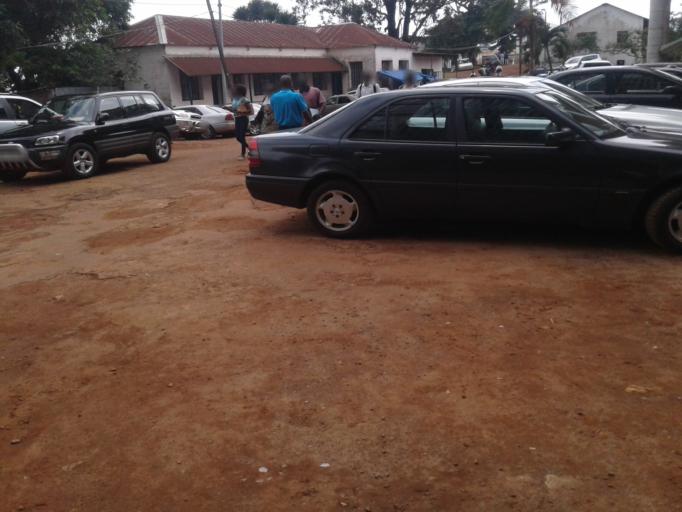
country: SL
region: Western Area
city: Freetown
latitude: 8.4779
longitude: -13.2216
